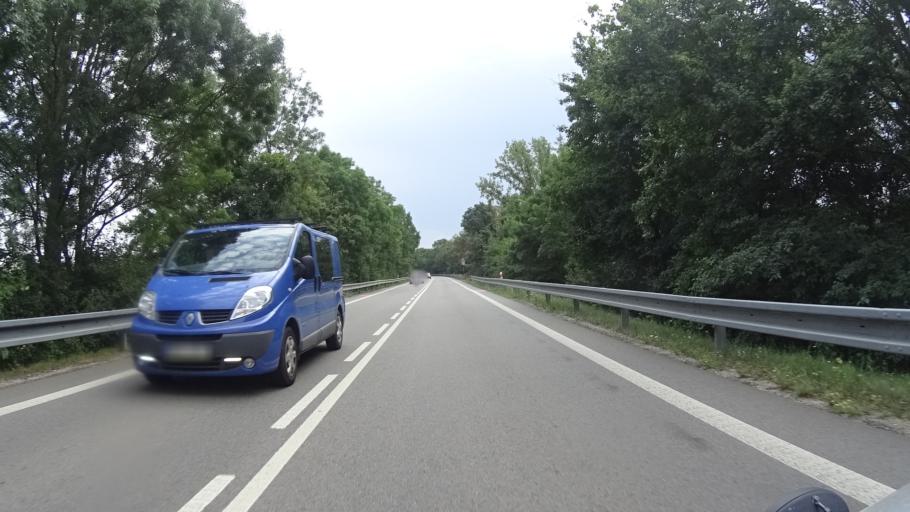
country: CZ
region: South Moravian
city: Podivin
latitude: 48.8177
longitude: 16.8268
